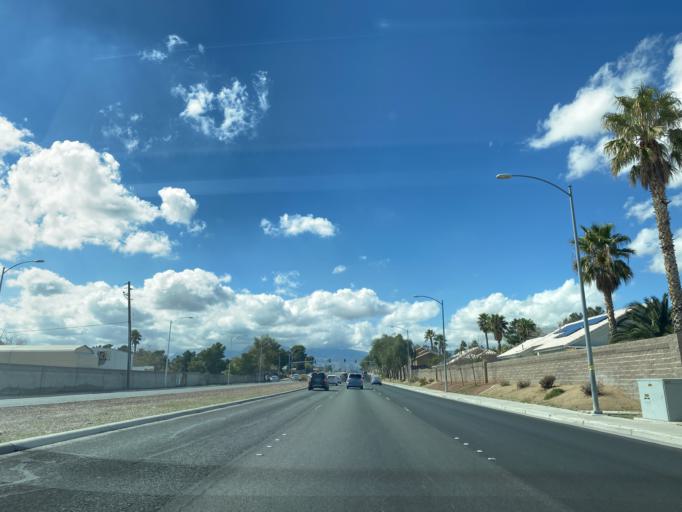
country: US
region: Nevada
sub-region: Clark County
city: Las Vegas
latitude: 36.2390
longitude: -115.2169
